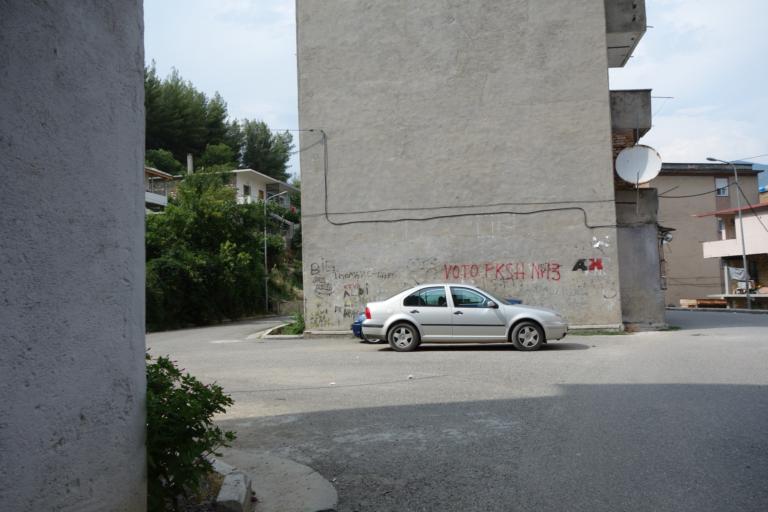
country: AL
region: Gjirokaster
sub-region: Rrethi i Permetit
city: Permet
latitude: 40.2349
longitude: 20.3505
